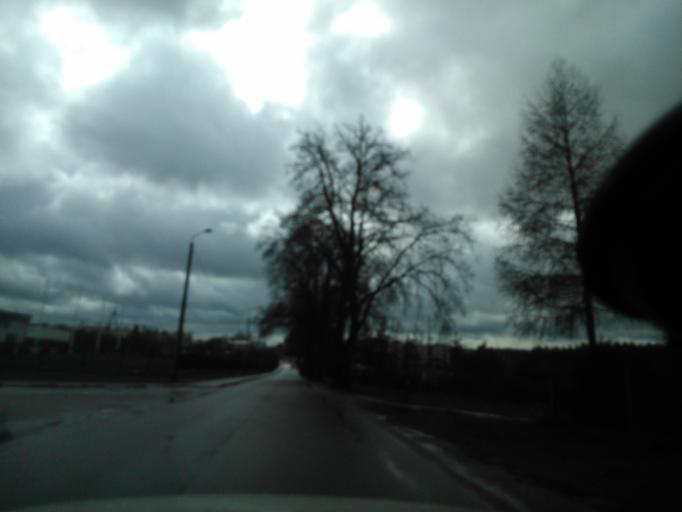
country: PL
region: Warmian-Masurian Voivodeship
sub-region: Powiat dzialdowski
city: Lidzbark
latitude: 53.2702
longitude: 19.8323
